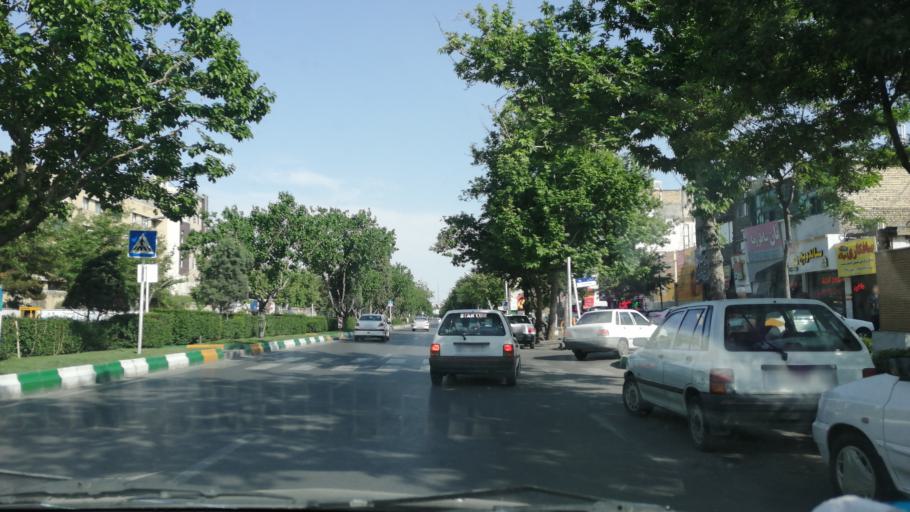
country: IR
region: Razavi Khorasan
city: Mashhad
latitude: 36.3132
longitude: 59.5624
